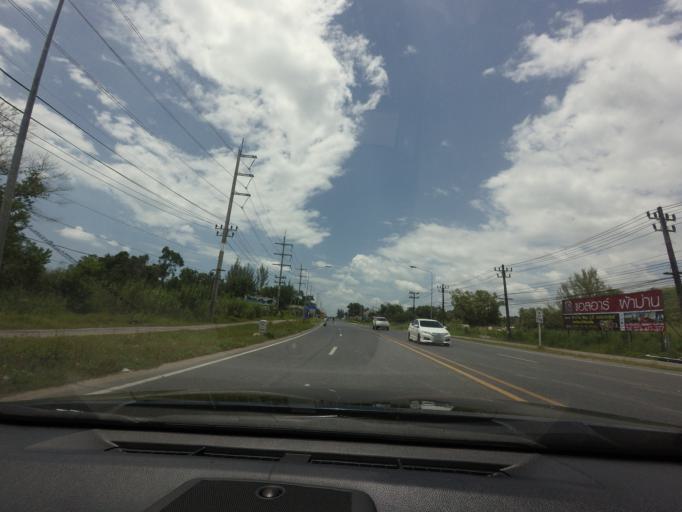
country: TH
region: Phangnga
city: Ban Khao Lak
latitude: 8.6542
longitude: 98.2535
